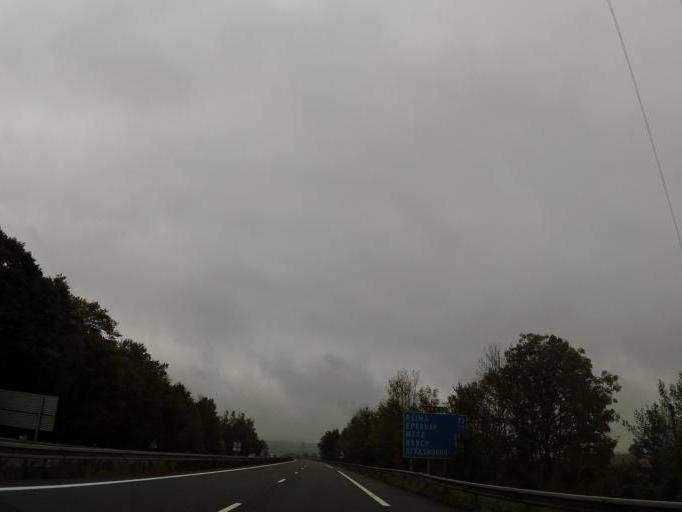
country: FR
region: Picardie
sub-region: Departement de l'Aisne
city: Montreuil-aux-Lions
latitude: 49.0177
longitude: 3.1581
